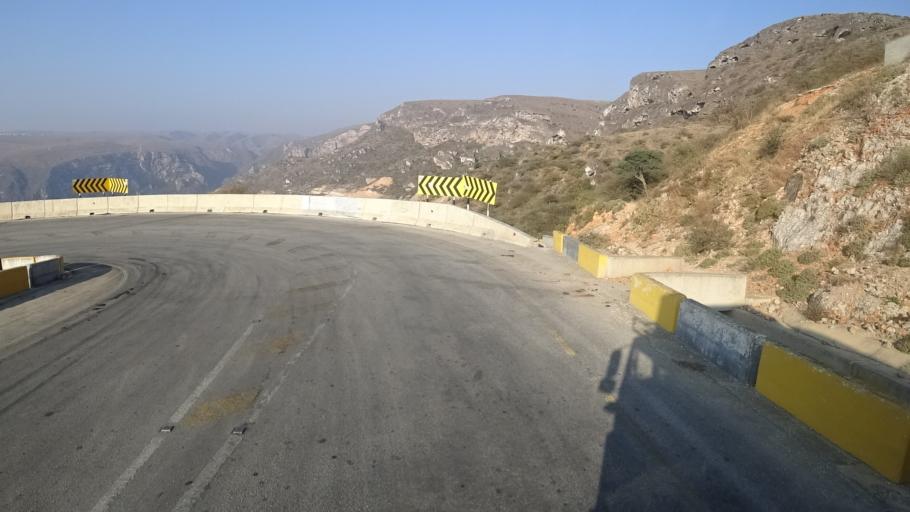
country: YE
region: Al Mahrah
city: Hawf
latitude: 16.7563
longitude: 53.2318
